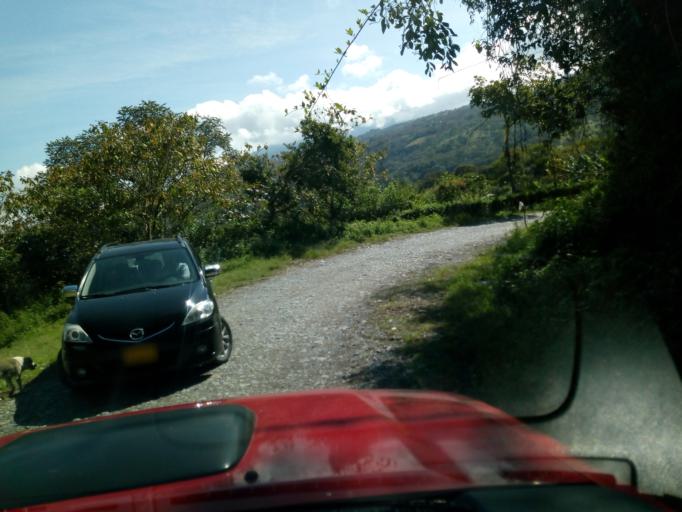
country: CO
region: Boyaca
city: Moniquira
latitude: 5.8953
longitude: -73.5323
